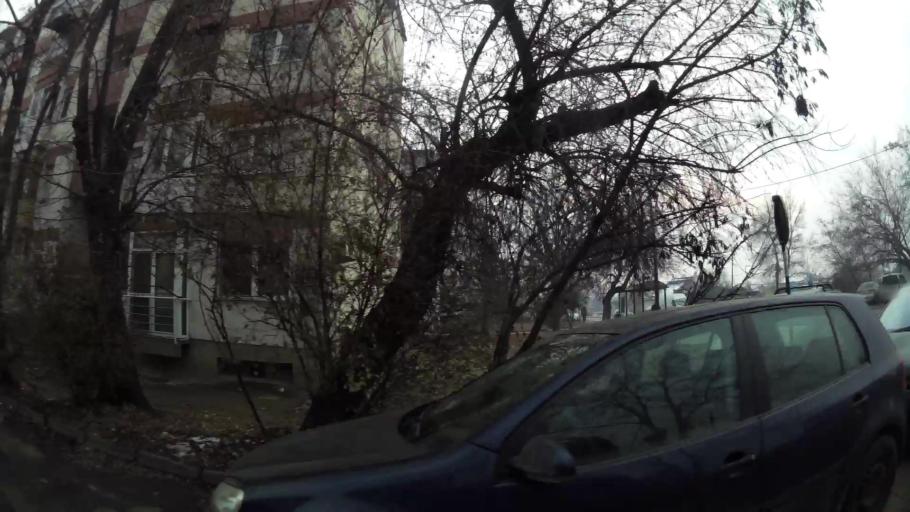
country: MK
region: Kisela Voda
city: Kisela Voda
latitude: 41.9976
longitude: 21.4948
